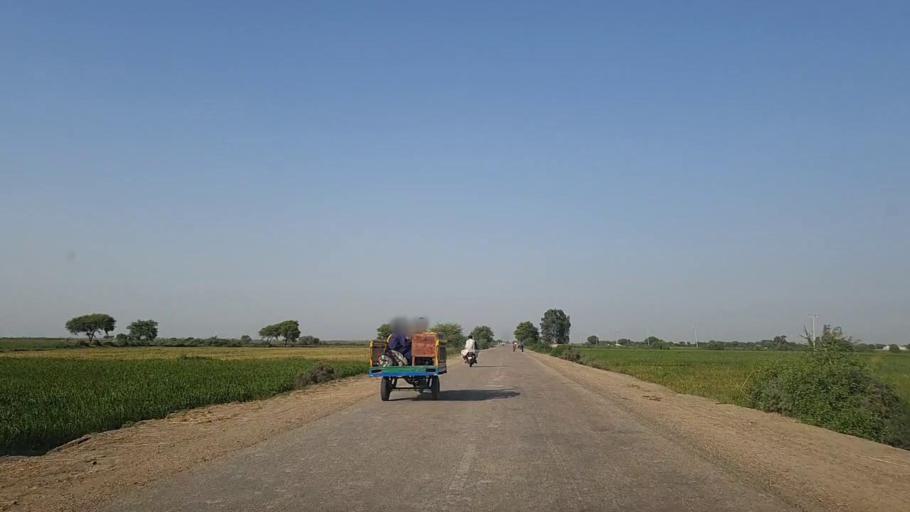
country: PK
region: Sindh
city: Mirpur Batoro
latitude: 24.5855
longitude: 68.3970
